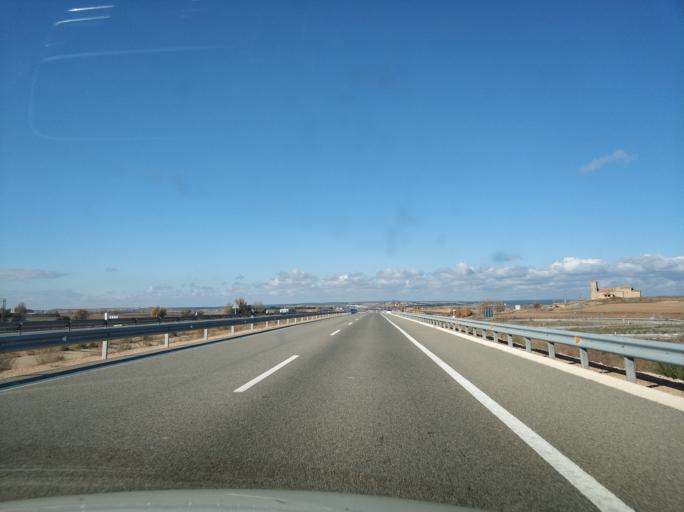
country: ES
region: Castille and Leon
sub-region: Provincia de Soria
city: Frechilla de Almazan
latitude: 41.4455
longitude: -2.5058
